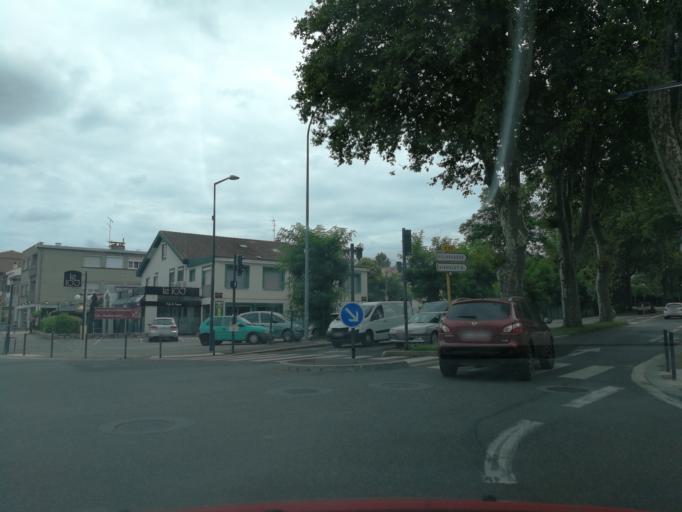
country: FR
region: Midi-Pyrenees
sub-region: Departement de la Haute-Garonne
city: Ramonville-Saint-Agne
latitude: 43.5404
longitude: 1.4790
